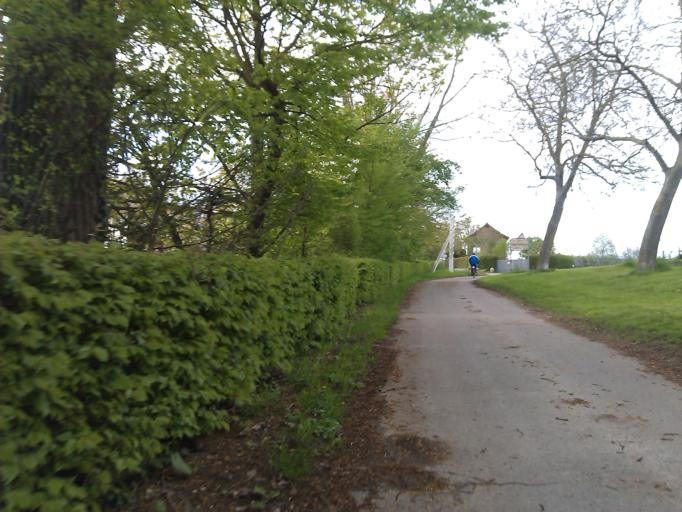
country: DE
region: Baden-Wuerttemberg
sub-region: Regierungsbezirk Stuttgart
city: Lauffen am Neckar
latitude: 49.0991
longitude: 9.1546
